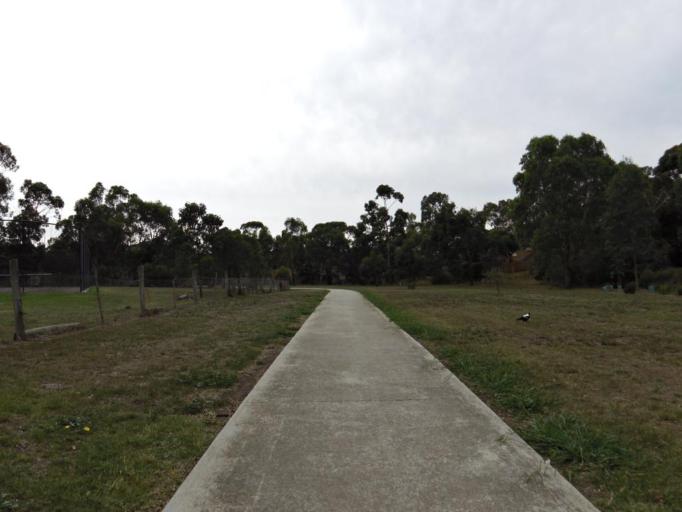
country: AU
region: Victoria
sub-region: Hume
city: Sunbury
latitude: -37.5625
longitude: 144.7237
